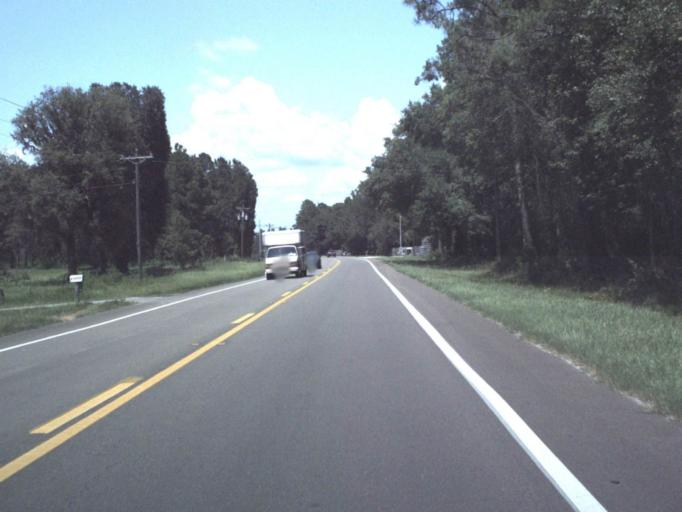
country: US
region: Florida
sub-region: Gilchrist County
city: Trenton
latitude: 29.6361
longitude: -82.7977
